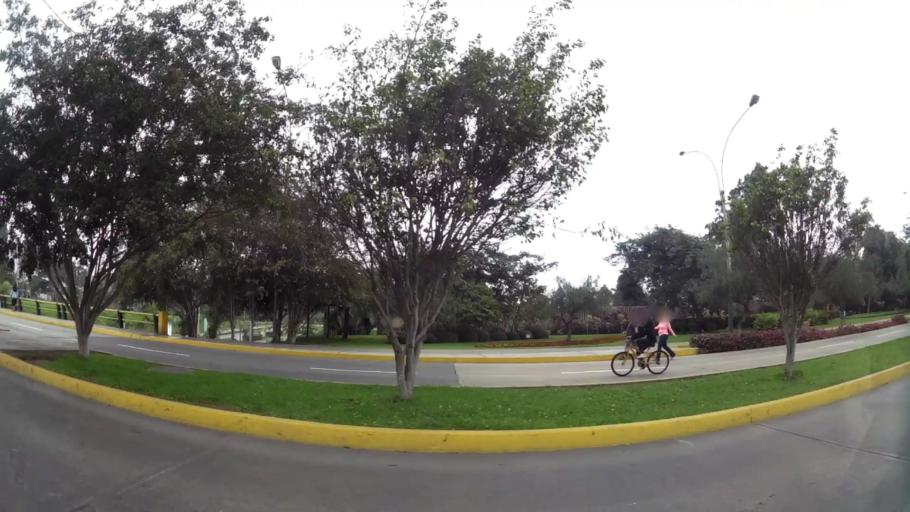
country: PE
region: Lima
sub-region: Lima
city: San Luis
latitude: -12.1021
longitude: -76.9803
